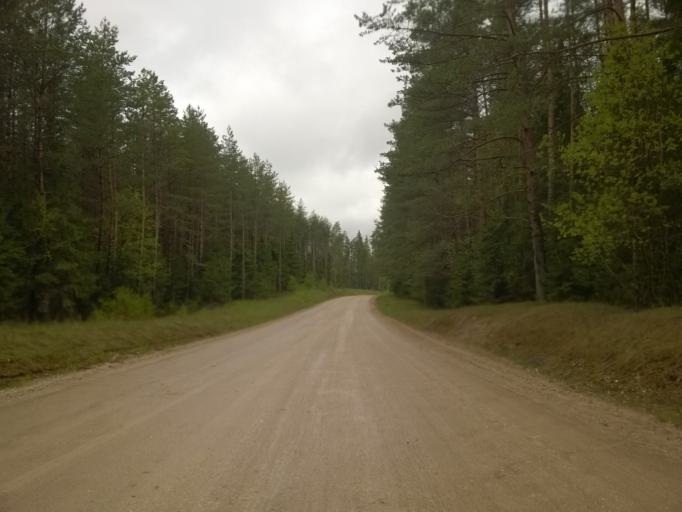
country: LV
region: Amatas Novads
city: Drabesi
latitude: 57.2147
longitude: 25.2324
